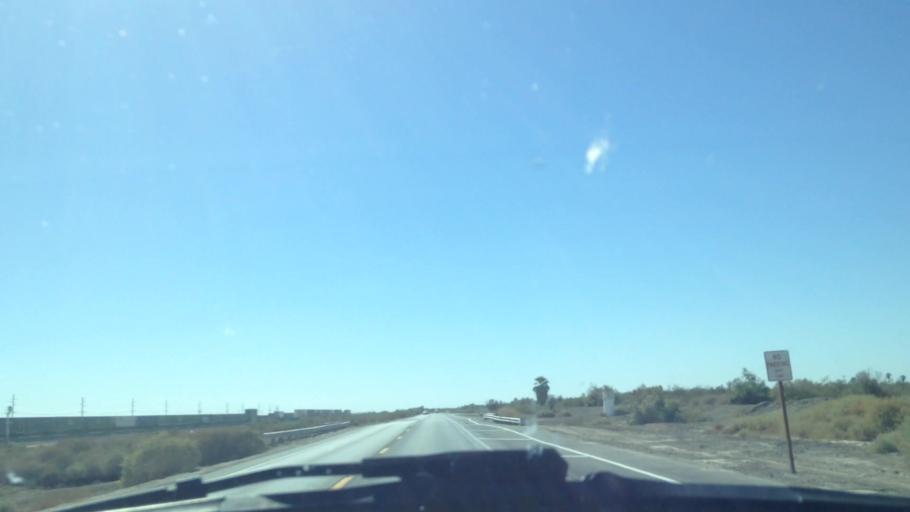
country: US
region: California
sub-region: Riverside County
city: Mecca
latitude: 33.5655
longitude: -116.0752
